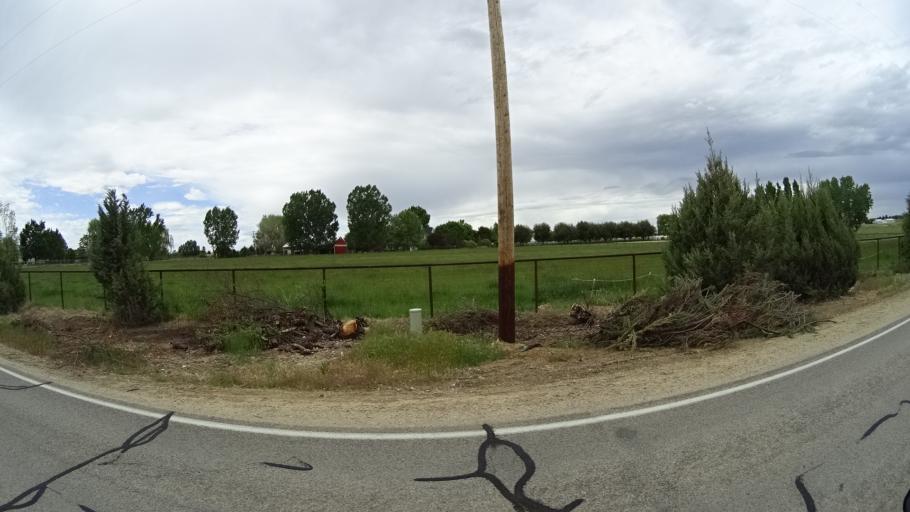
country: US
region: Idaho
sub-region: Ada County
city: Meridian
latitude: 43.5562
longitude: -116.4138
